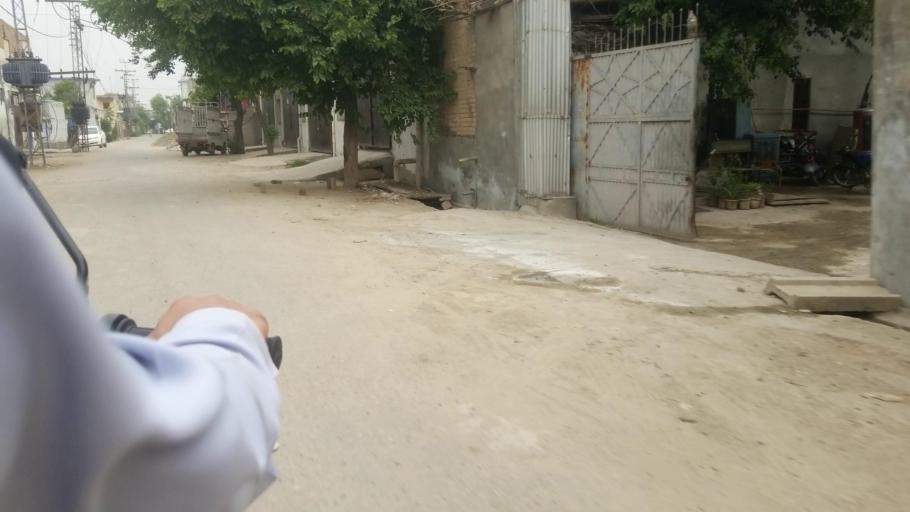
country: PK
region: Khyber Pakhtunkhwa
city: Peshawar
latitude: 33.9804
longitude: 71.5581
